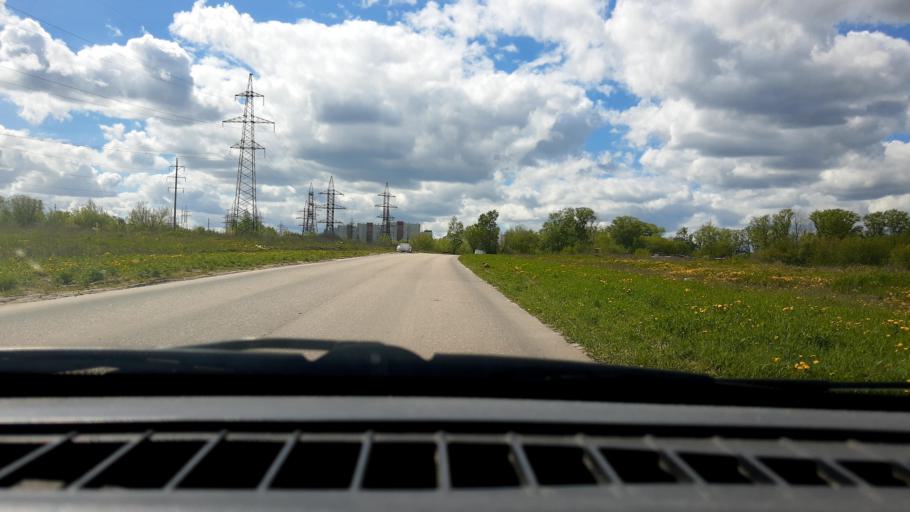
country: RU
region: Nizjnij Novgorod
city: Afonino
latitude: 56.2682
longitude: 44.0391
